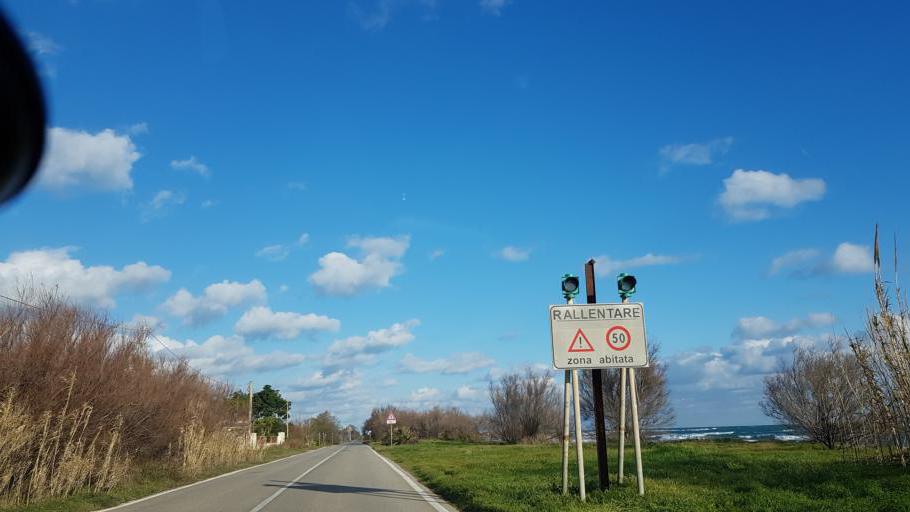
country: IT
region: Apulia
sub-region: Provincia di Brindisi
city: Materdomini
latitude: 40.6702
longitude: 17.9464
